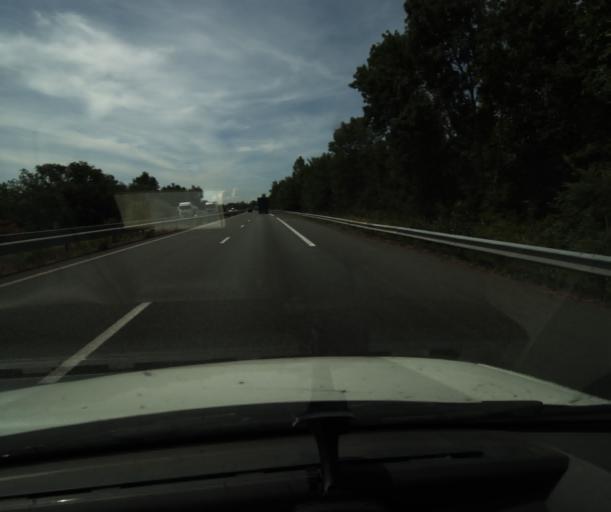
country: FR
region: Languedoc-Roussillon
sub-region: Departement de l'Aude
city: Saint-Martin-Lalande
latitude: 43.2807
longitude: 1.9836
